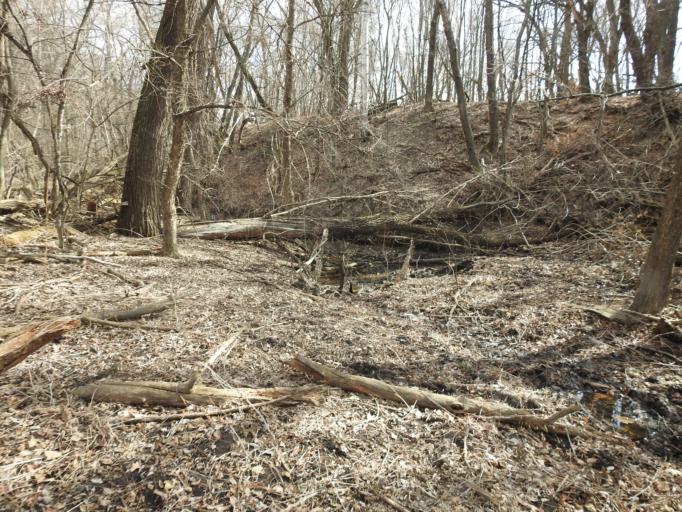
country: RU
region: Saratov
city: Krasnyy Oktyabr'
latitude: 51.3833
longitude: 45.7756
